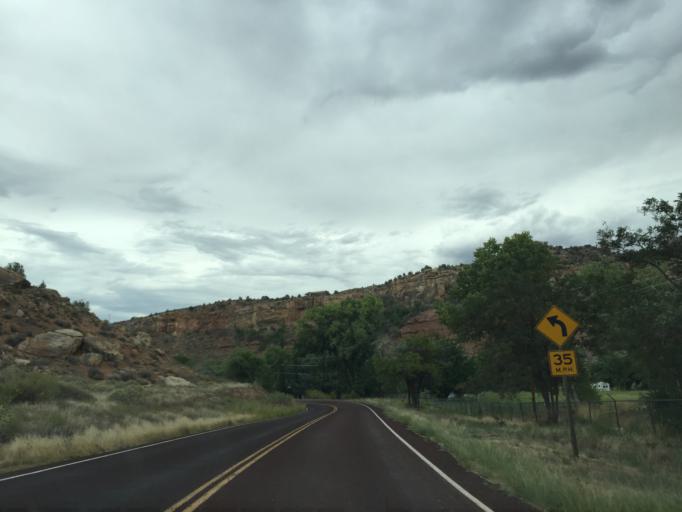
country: US
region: Utah
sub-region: Washington County
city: Hildale
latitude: 37.1608
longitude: -113.0313
